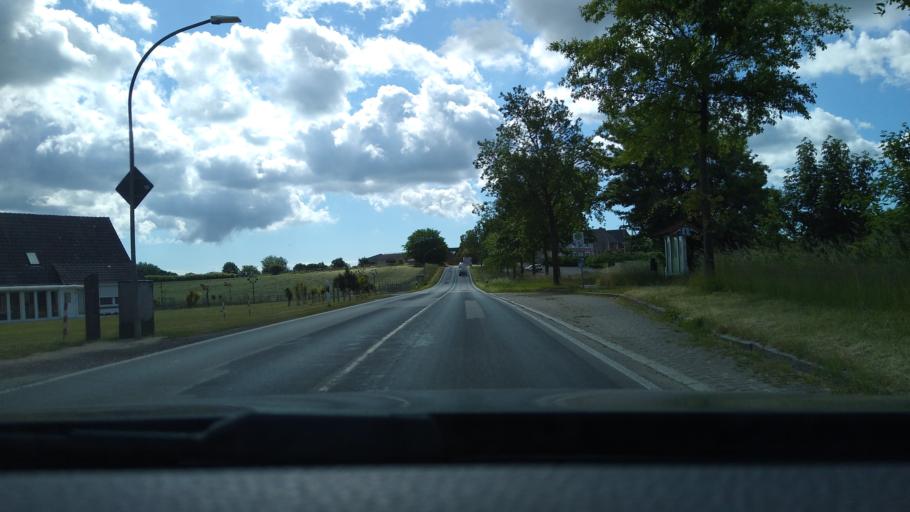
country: DE
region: Schleswig-Holstein
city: Kabelhorst
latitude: 54.2150
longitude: 10.9227
